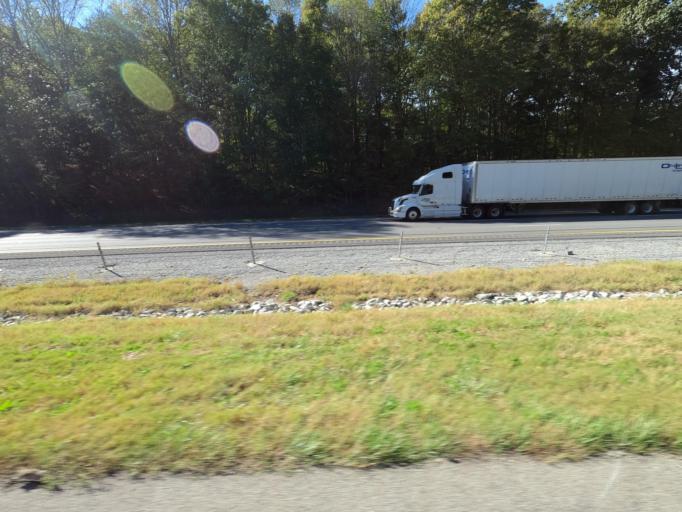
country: US
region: Tennessee
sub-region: Dickson County
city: White Bluff
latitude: 36.0265
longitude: -87.1975
